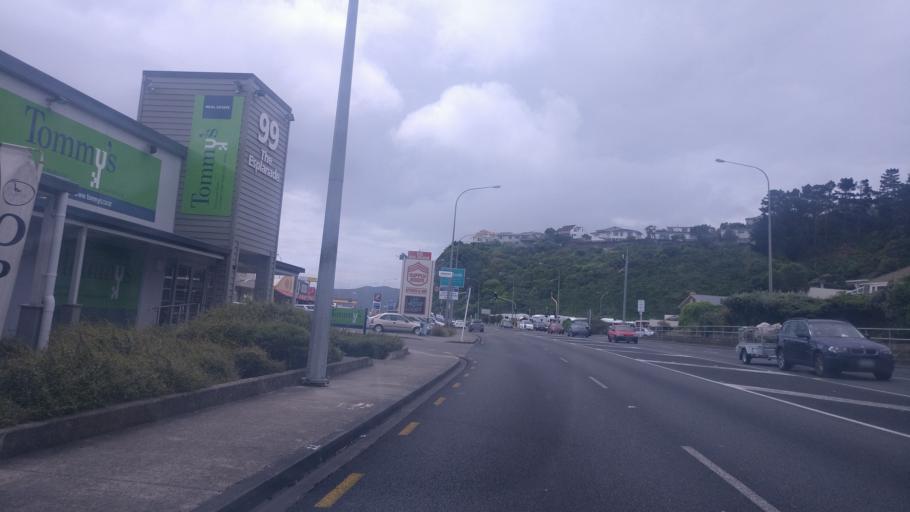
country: NZ
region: Wellington
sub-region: Porirua City
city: Porirua
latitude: -41.0931
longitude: 174.8687
